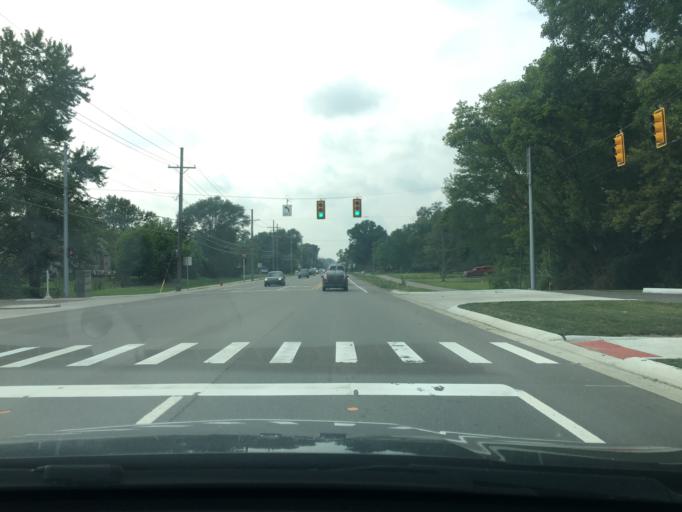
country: US
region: Michigan
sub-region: Oakland County
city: Rochester Hills
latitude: 42.6354
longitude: -83.1600
